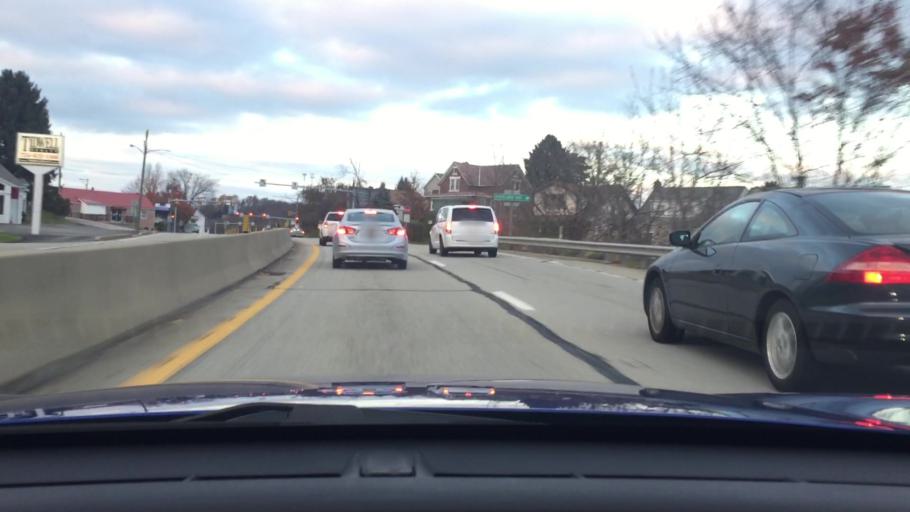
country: US
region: Pennsylvania
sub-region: Westmoreland County
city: South Greensburg
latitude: 40.2720
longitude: -79.5556
